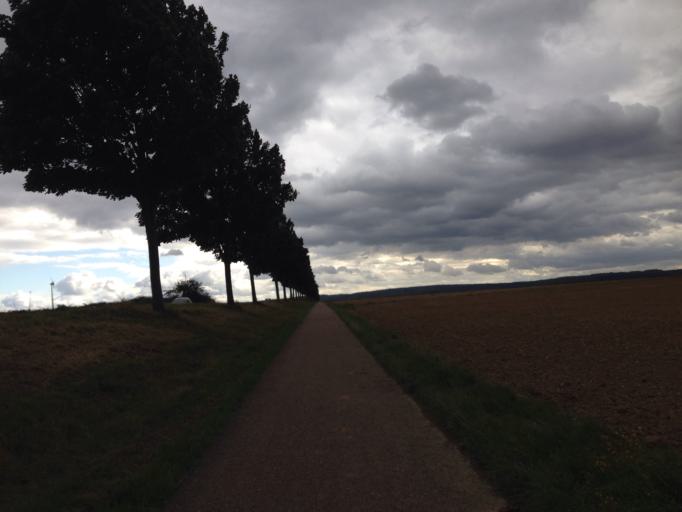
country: DE
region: Hesse
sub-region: Regierungsbezirk Giessen
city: Limburg an der Lahn
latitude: 50.3699
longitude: 8.0615
